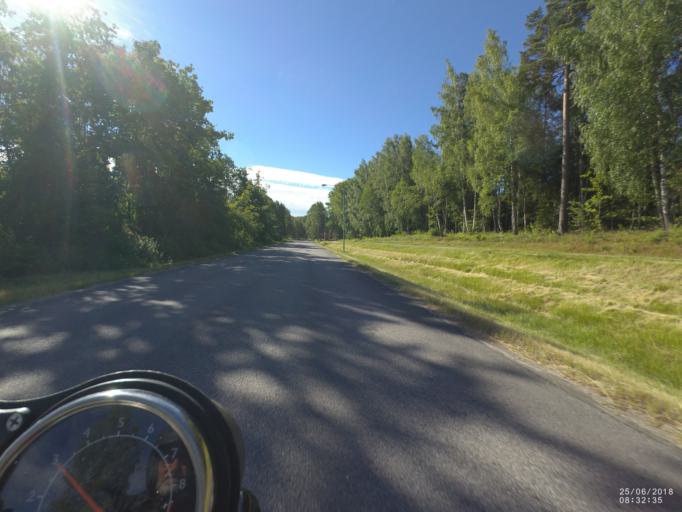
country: SE
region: Soedermanland
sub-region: Nykopings Kommun
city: Nykoping
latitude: 58.7308
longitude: 17.0278
